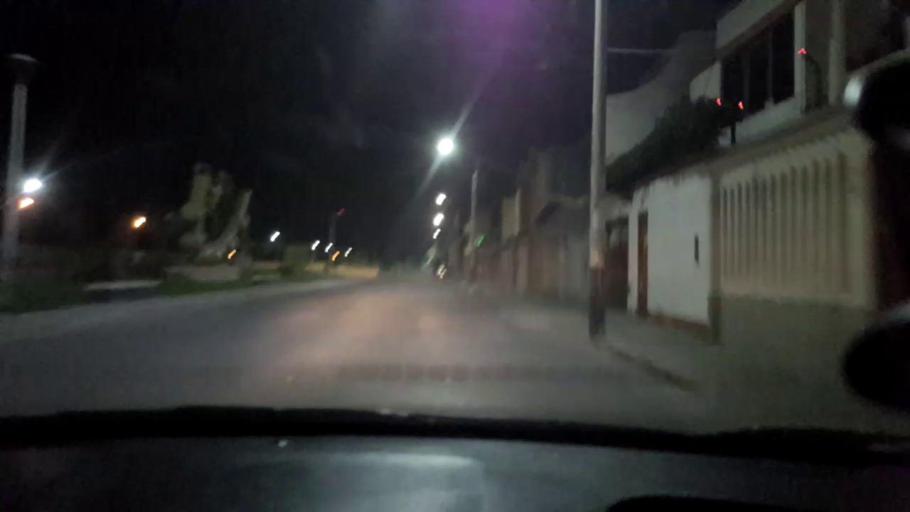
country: PE
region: Lambayeque
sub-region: Provincia de Chiclayo
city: Chiclayo
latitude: -6.7859
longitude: -79.8390
